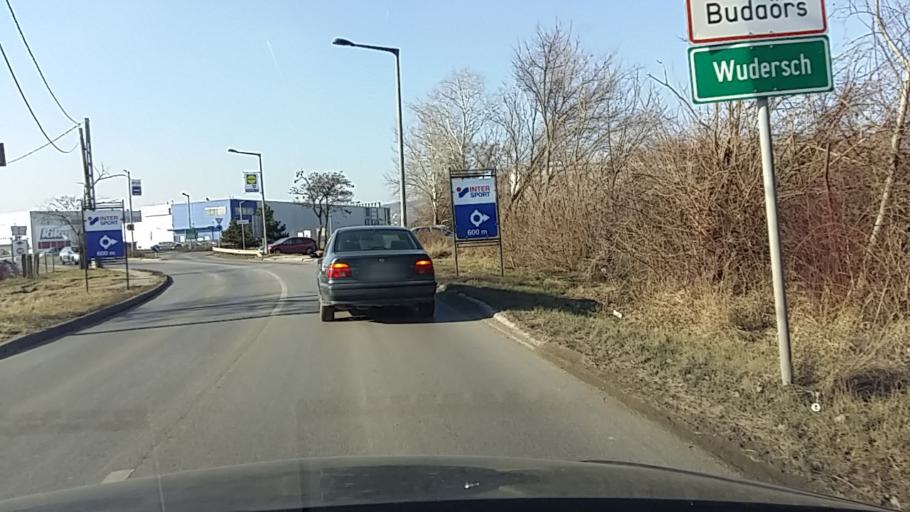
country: HU
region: Pest
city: Budaors
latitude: 47.4498
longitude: 18.9721
